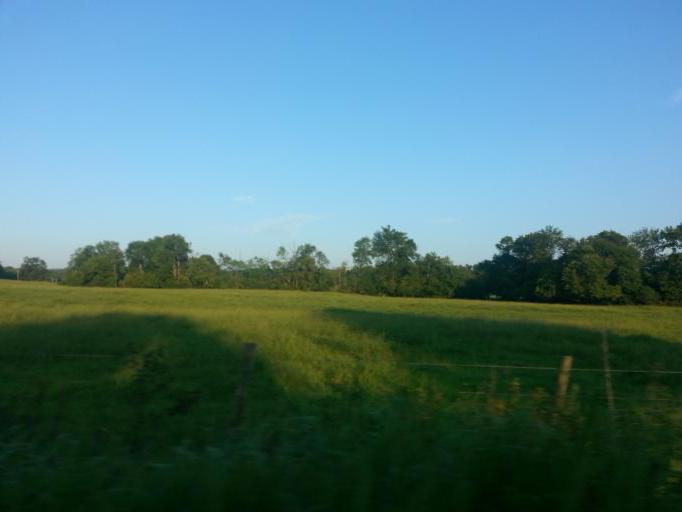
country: US
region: Tennessee
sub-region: Rhea County
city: Spring City
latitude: 35.6659
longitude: -84.6767
